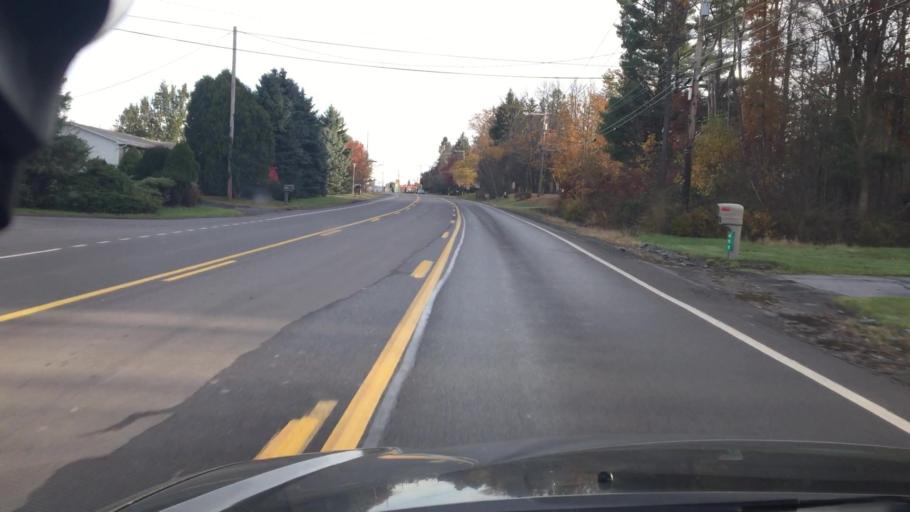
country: US
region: Pennsylvania
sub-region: Luzerne County
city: Mountain Top
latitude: 41.1164
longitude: -75.9122
